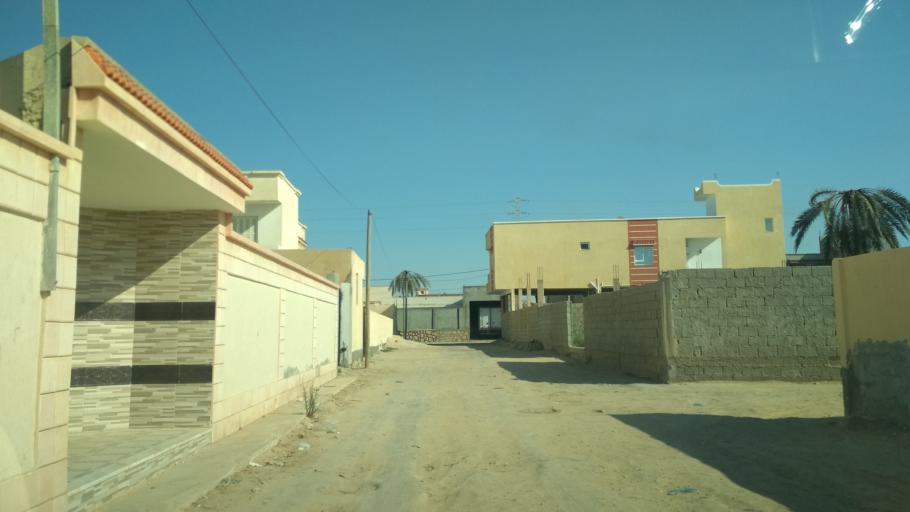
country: TN
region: Qabis
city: Gabes
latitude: 33.9467
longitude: 10.0603
